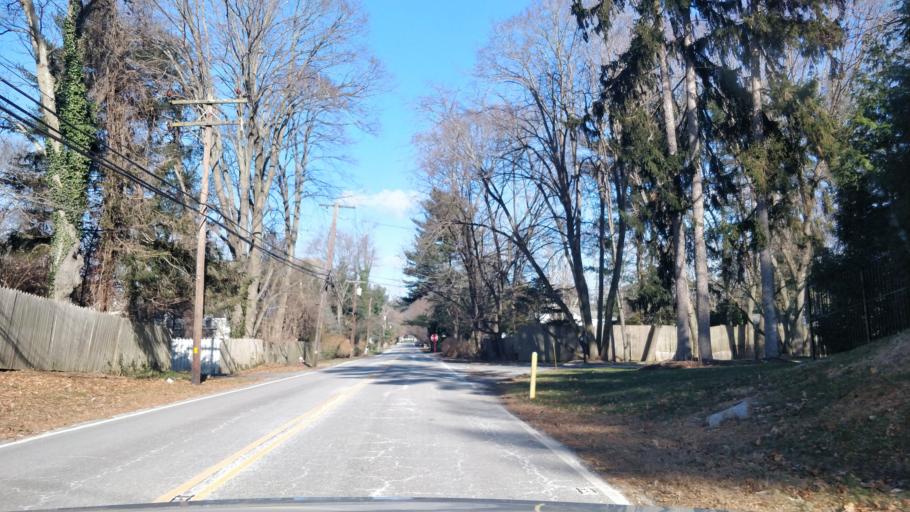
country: US
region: New York
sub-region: Nassau County
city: East Hills
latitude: 40.7874
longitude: -73.6148
